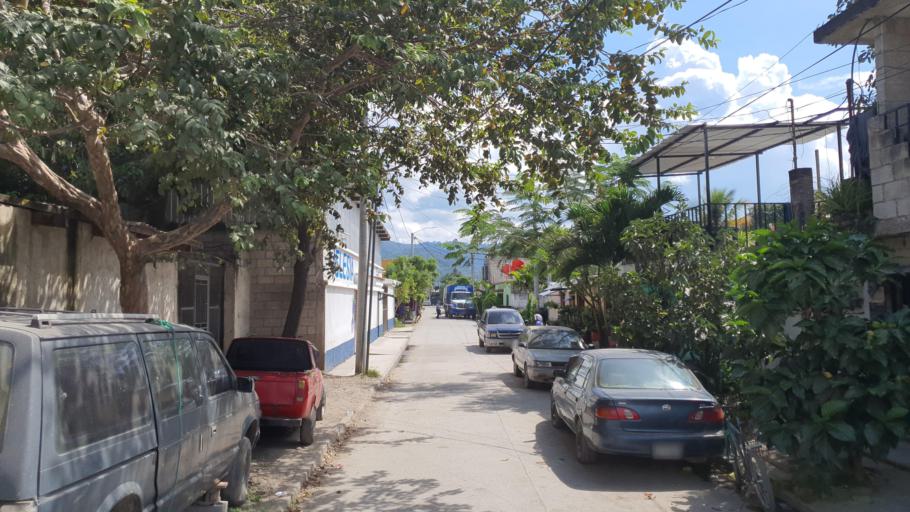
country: GT
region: Guatemala
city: Villa Canales
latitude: 14.4621
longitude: -90.5590
